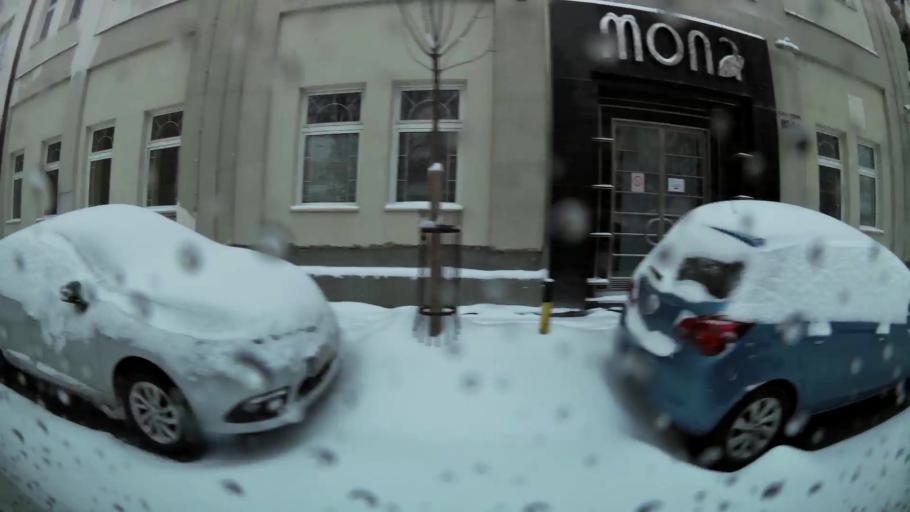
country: RS
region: Central Serbia
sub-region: Belgrade
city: Stari Grad
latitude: 44.8270
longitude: 20.4603
